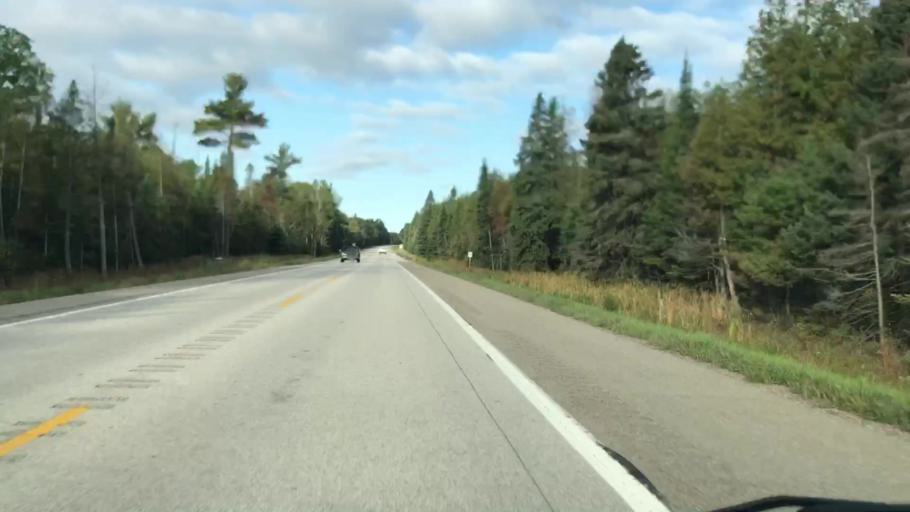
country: US
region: Michigan
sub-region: Luce County
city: Newberry
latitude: 46.3320
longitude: -85.0751
